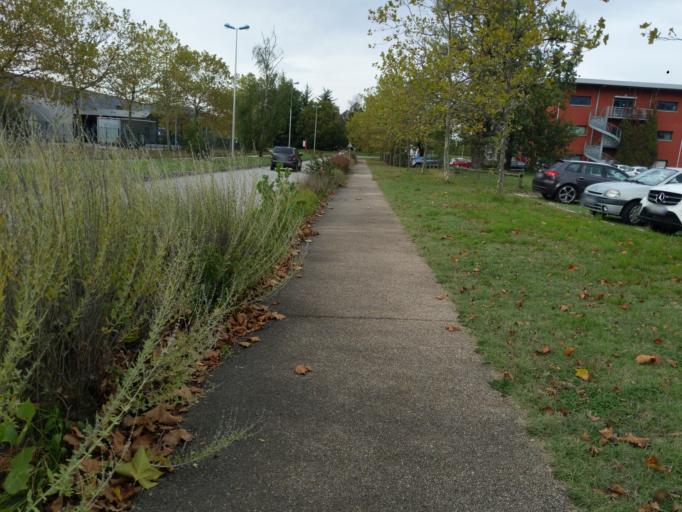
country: FR
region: Rhone-Alpes
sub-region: Departement de la Savoie
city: Montmelian
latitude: 45.4778
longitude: 6.0309
